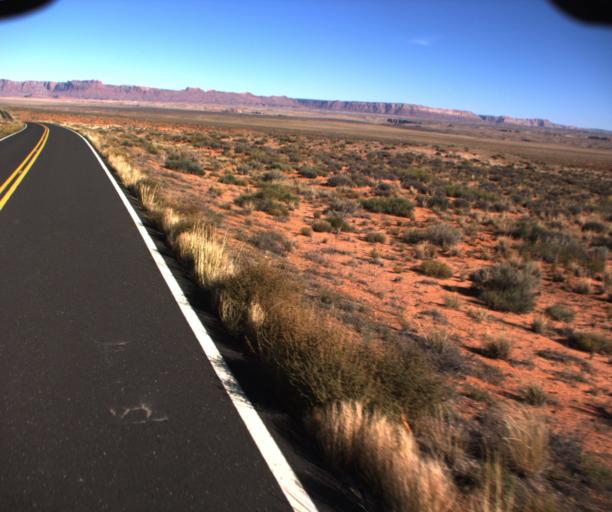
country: US
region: Arizona
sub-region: Coconino County
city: Page
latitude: 36.6835
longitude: -111.8479
